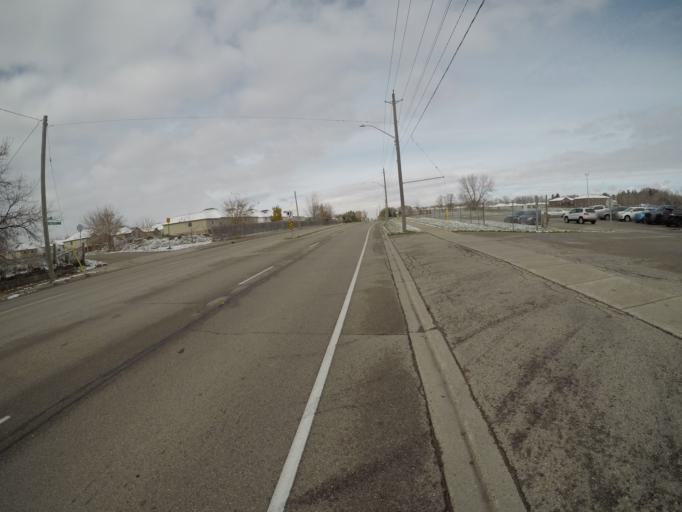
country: CA
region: Ontario
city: Waterloo
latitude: 43.4963
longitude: -80.4908
